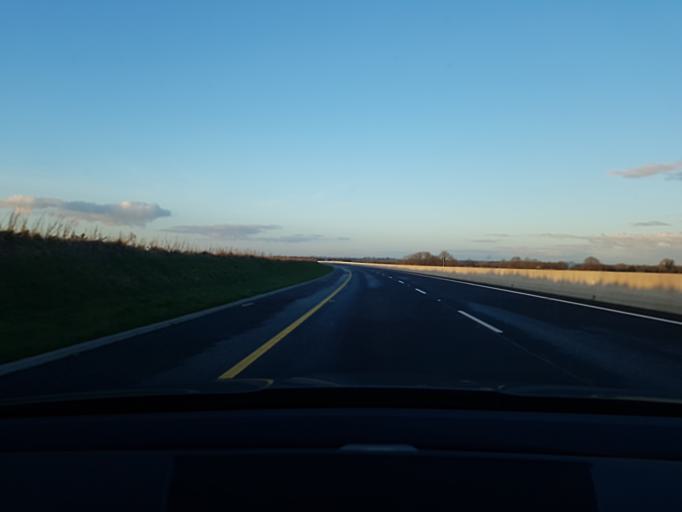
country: IE
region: Connaught
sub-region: County Galway
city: Tuam
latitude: 53.4537
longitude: -8.8476
